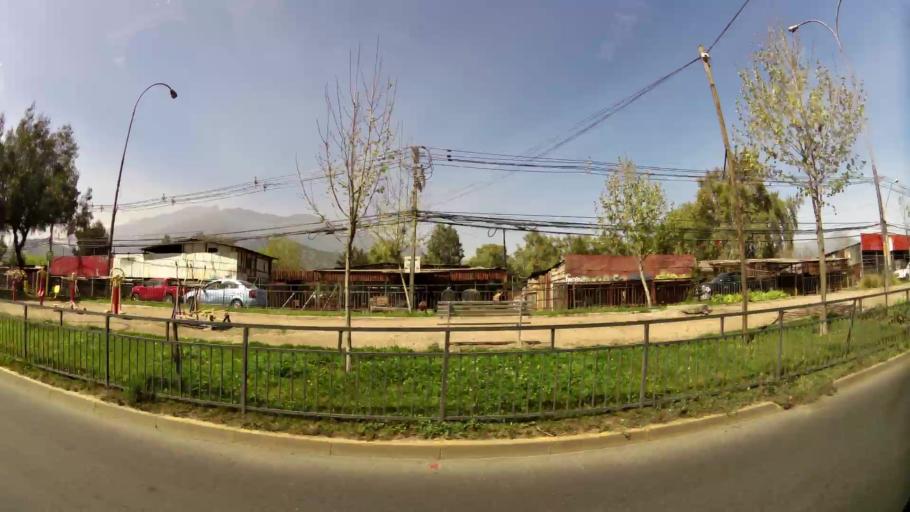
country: CL
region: Santiago Metropolitan
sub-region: Provincia de Cordillera
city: Puente Alto
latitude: -33.5703
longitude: -70.5534
